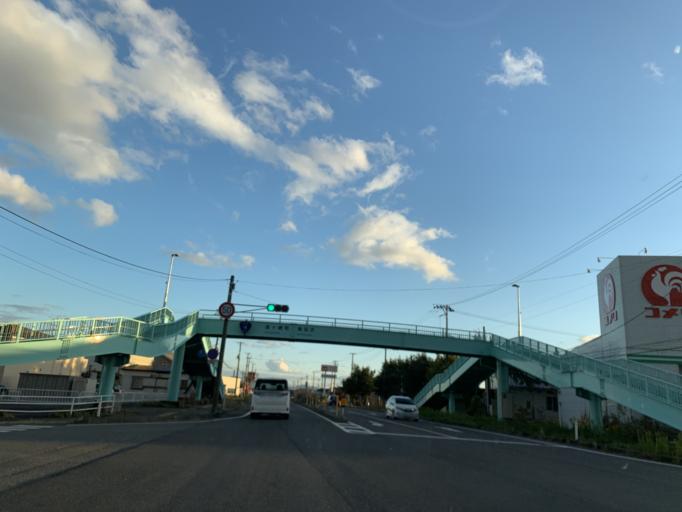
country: JP
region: Iwate
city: Mizusawa
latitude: 39.2016
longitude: 141.1100
